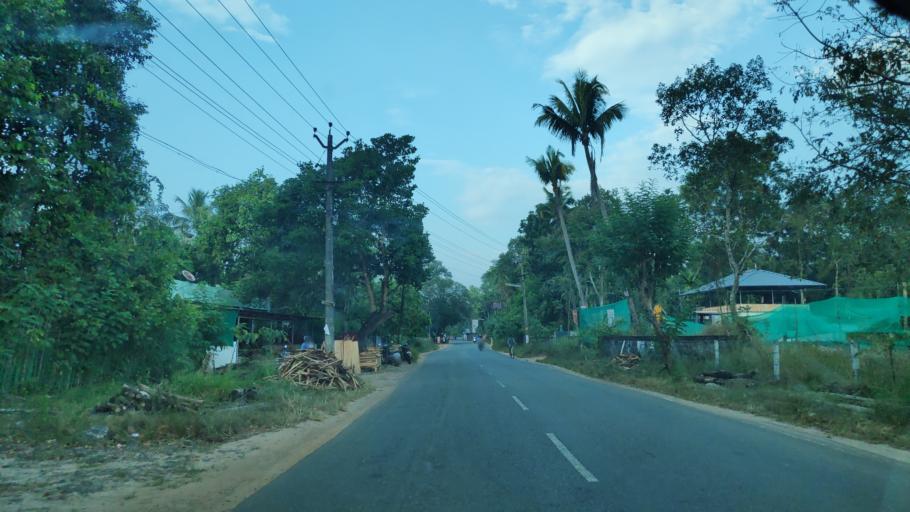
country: IN
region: Kerala
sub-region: Alappuzha
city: Shertallai
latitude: 9.6328
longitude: 76.3708
